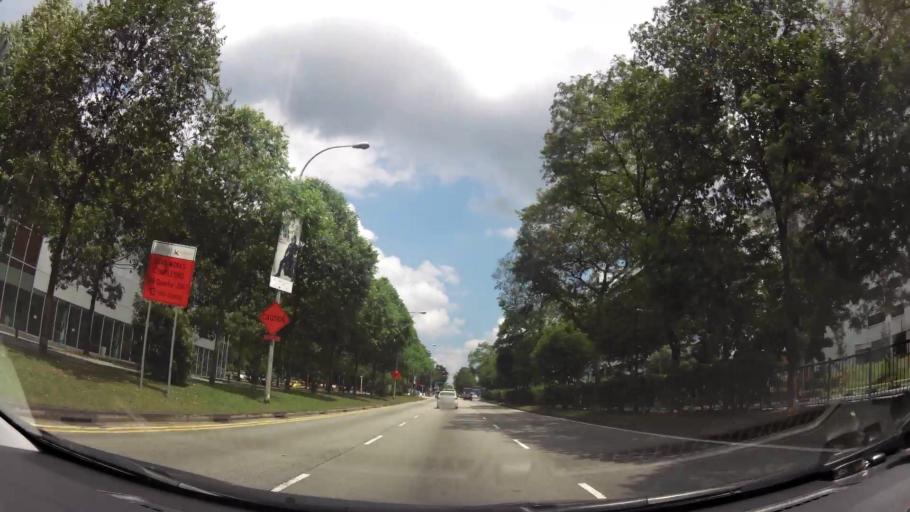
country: MY
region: Johor
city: Johor Bahru
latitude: 1.4429
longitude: 103.7870
